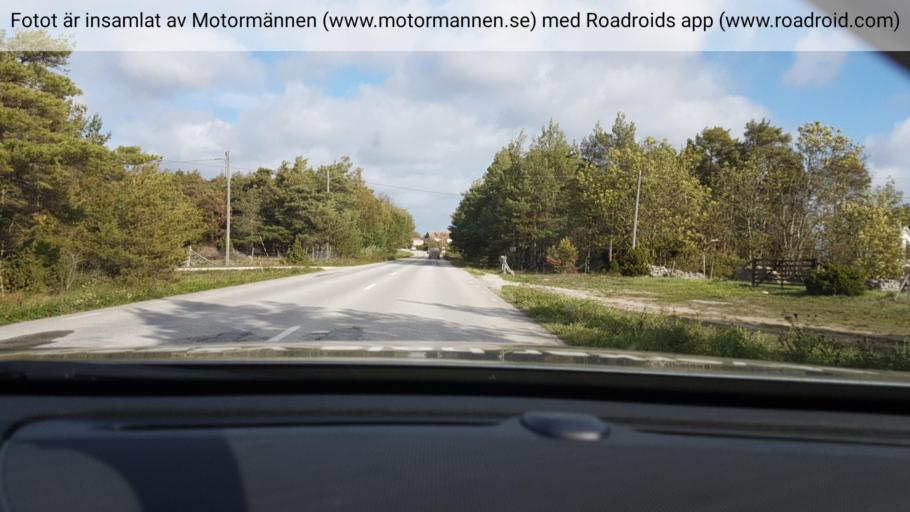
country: SE
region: Gotland
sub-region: Gotland
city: Slite
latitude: 57.8912
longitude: 19.0912
